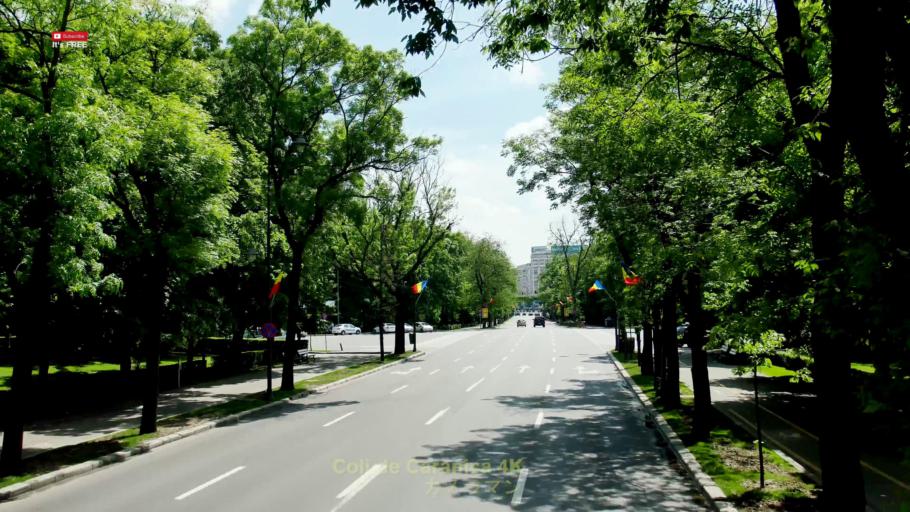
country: RO
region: Bucuresti
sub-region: Municipiul Bucuresti
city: Bucuresti
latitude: 44.4569
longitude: 26.0832
